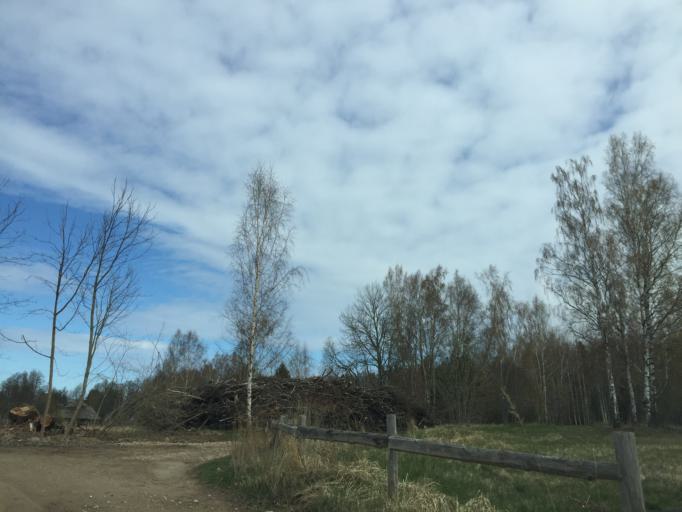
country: LV
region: Salacgrivas
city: Salacgriva
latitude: 57.5424
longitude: 24.3671
